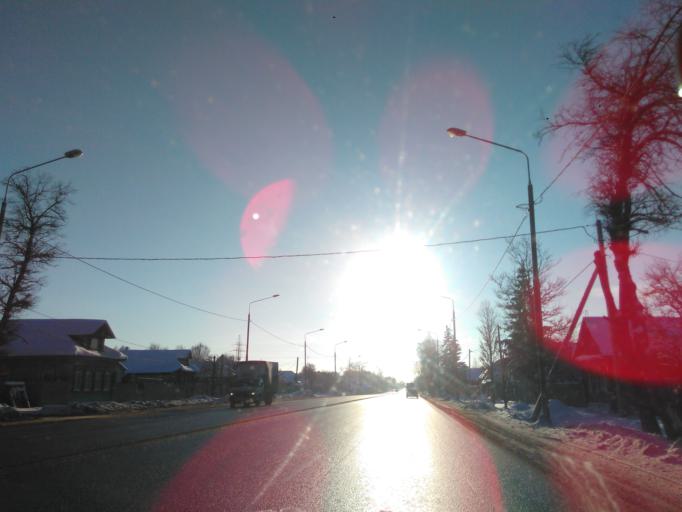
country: RU
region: Moskovskaya
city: Klin
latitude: 56.3859
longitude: 36.6680
